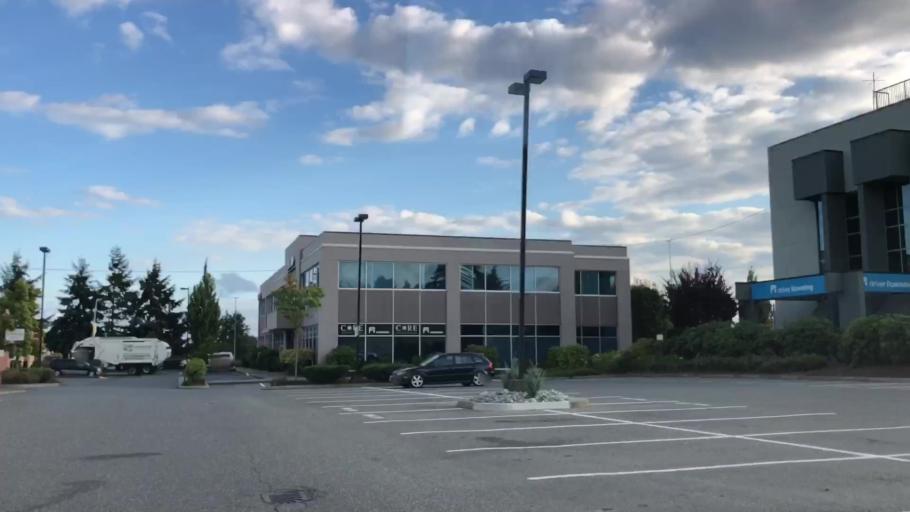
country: CA
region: British Columbia
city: Nanaimo
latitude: 49.2333
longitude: -124.0475
